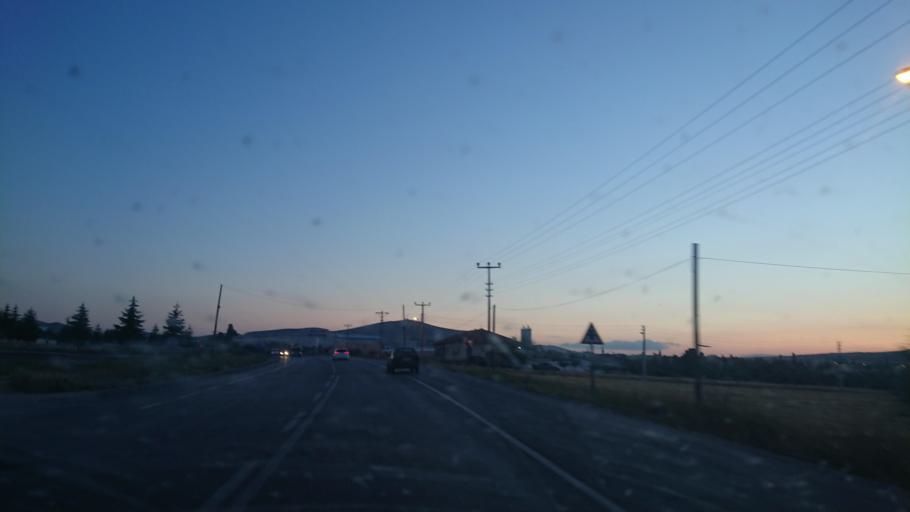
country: TR
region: Aksaray
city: Ortakoy
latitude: 38.7507
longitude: 34.0612
